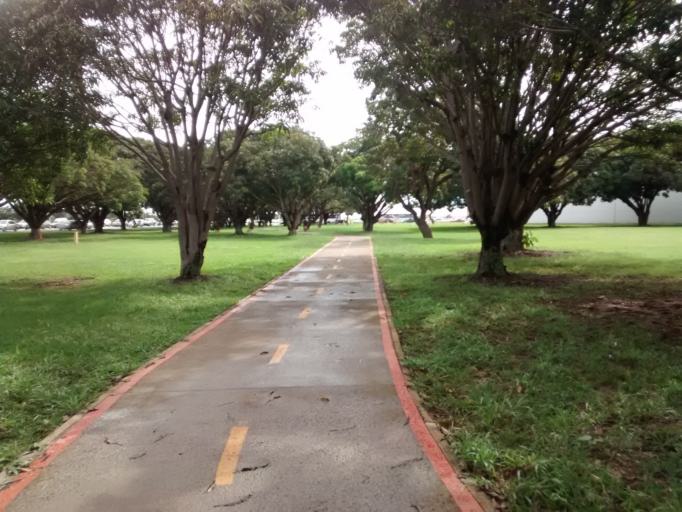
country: BR
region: Federal District
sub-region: Brasilia
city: Brasilia
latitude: -15.7855
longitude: -47.9105
